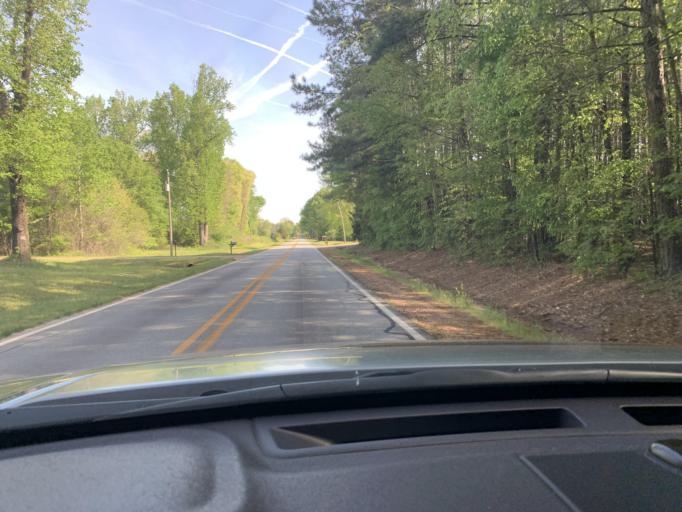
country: US
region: Georgia
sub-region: Oconee County
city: Watkinsville
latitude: 33.7979
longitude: -83.3200
